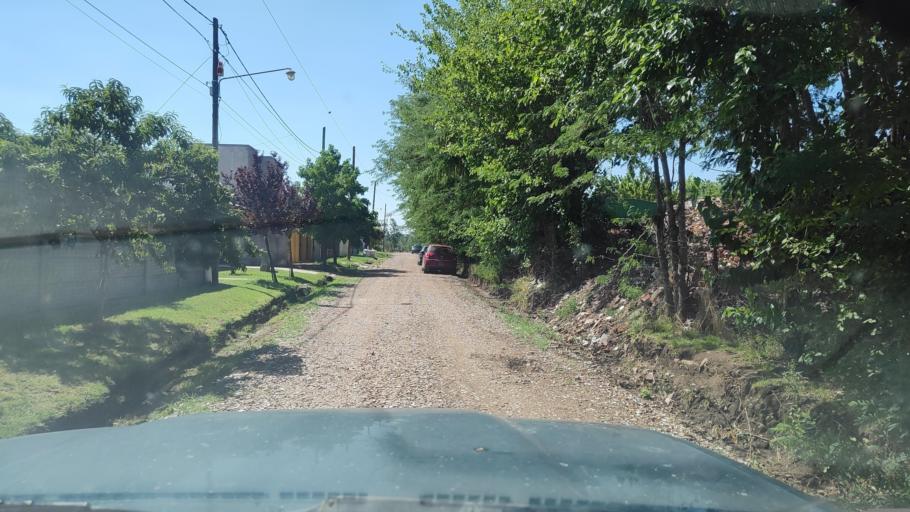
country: AR
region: Buenos Aires
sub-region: Partido de Lujan
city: Lujan
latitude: -34.5660
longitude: -59.1368
